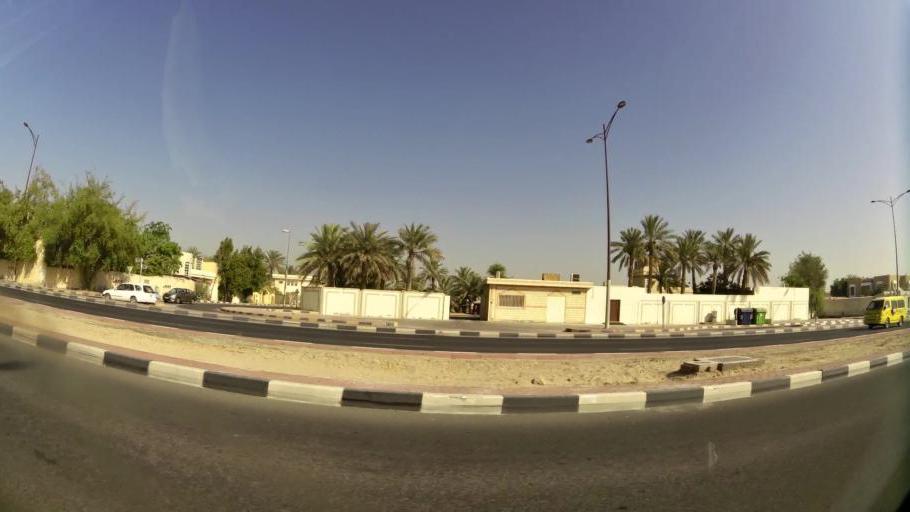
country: AE
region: Ash Shariqah
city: Sharjah
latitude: 25.3599
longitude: 55.4429
